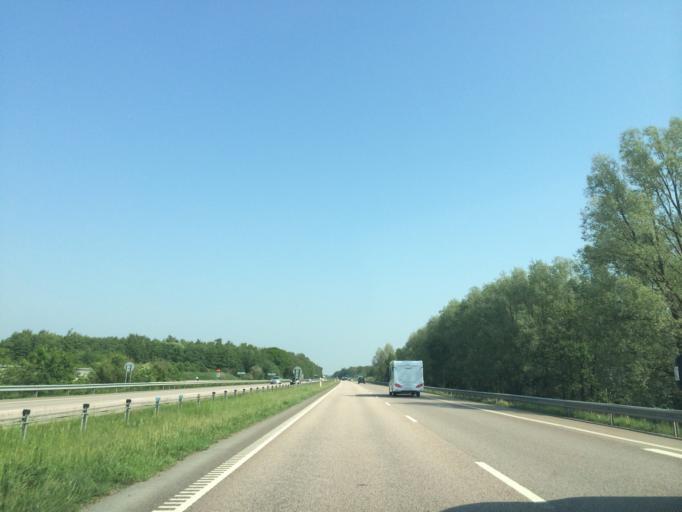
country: SE
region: Skane
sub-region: Helsingborg
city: Barslov
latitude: 56.0485
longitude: 12.7852
